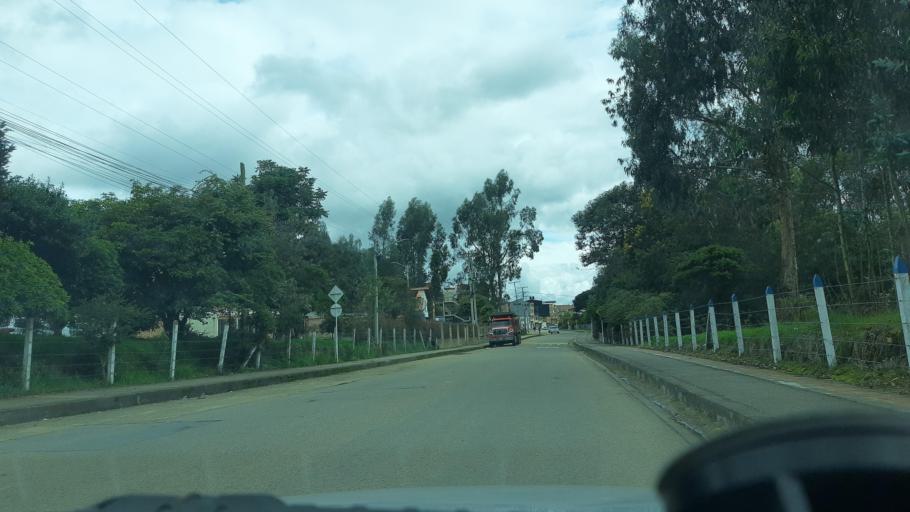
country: CO
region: Cundinamarca
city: Villapinzon
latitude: 5.2216
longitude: -73.5924
